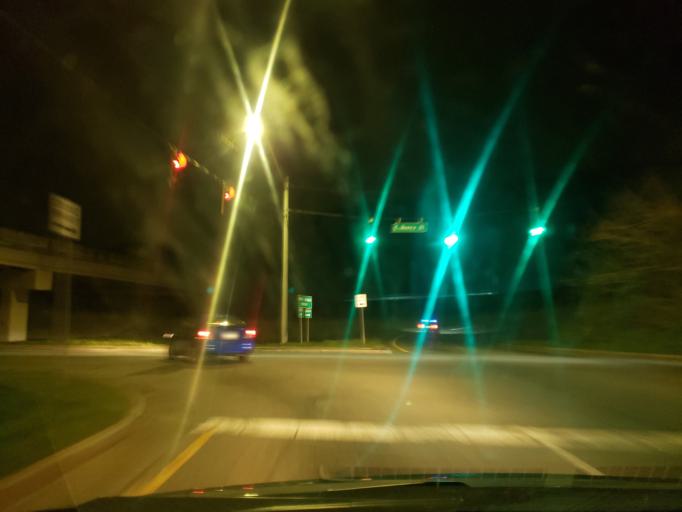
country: US
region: Georgia
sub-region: Chatham County
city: Thunderbolt
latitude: 32.0563
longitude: -81.0722
